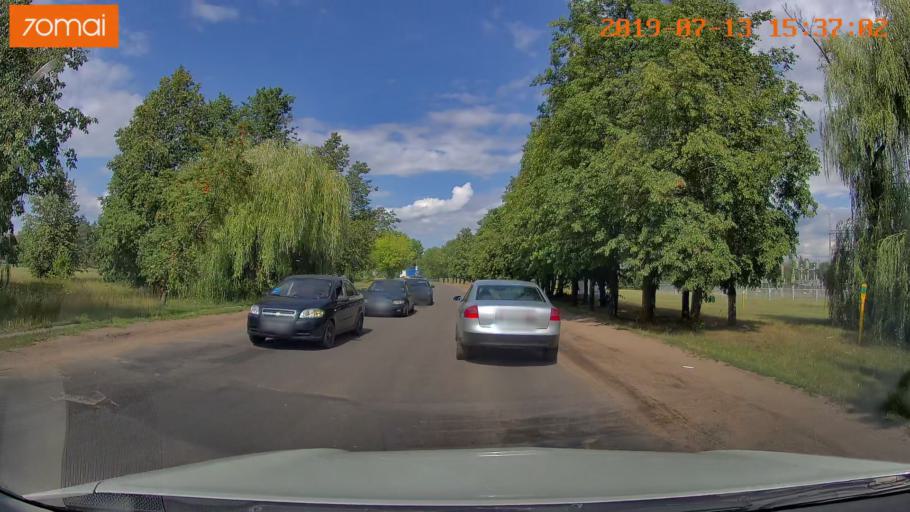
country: BY
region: Mogilev
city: Babruysk
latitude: 53.1356
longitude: 29.1678
